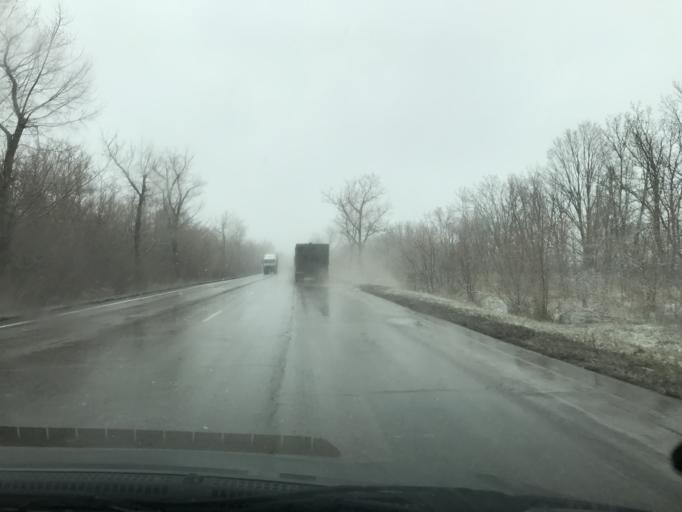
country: RU
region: Rostov
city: Bataysk
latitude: 47.0356
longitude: 39.8683
